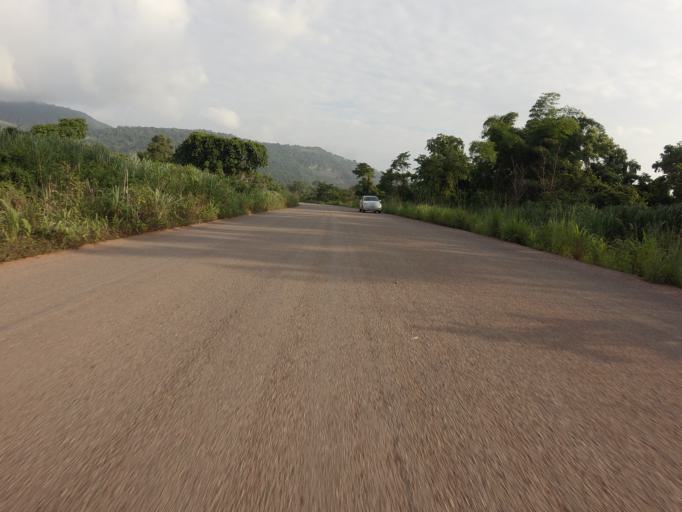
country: TG
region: Plateaux
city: Kpalime
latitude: 6.9343
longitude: 0.4629
